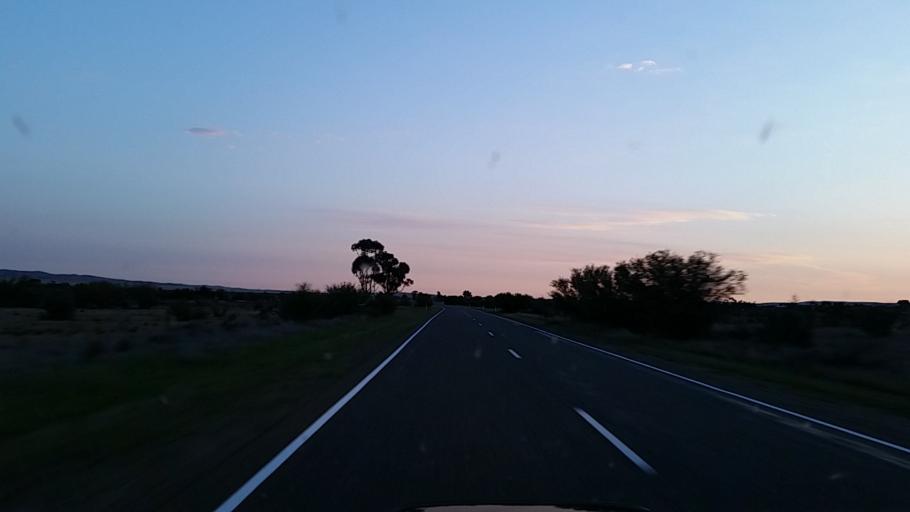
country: AU
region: South Australia
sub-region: Peterborough
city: Peterborough
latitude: -33.1444
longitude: 138.9284
